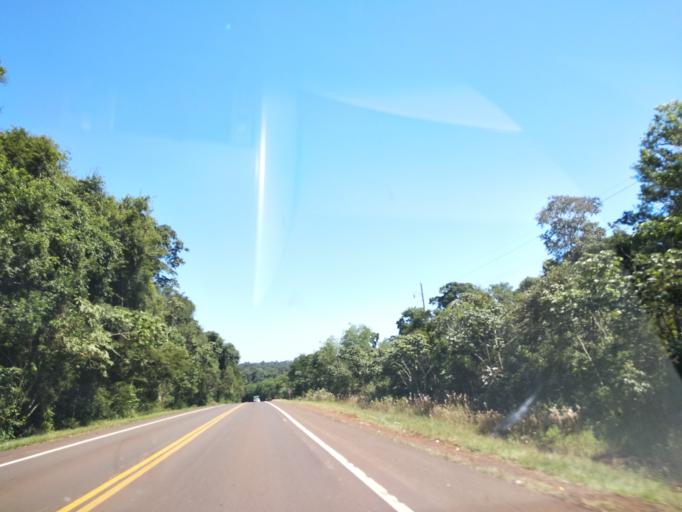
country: AR
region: Misiones
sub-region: Departamento de Iguazu
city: Puerto Iguazu
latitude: -25.6759
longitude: -54.5047
